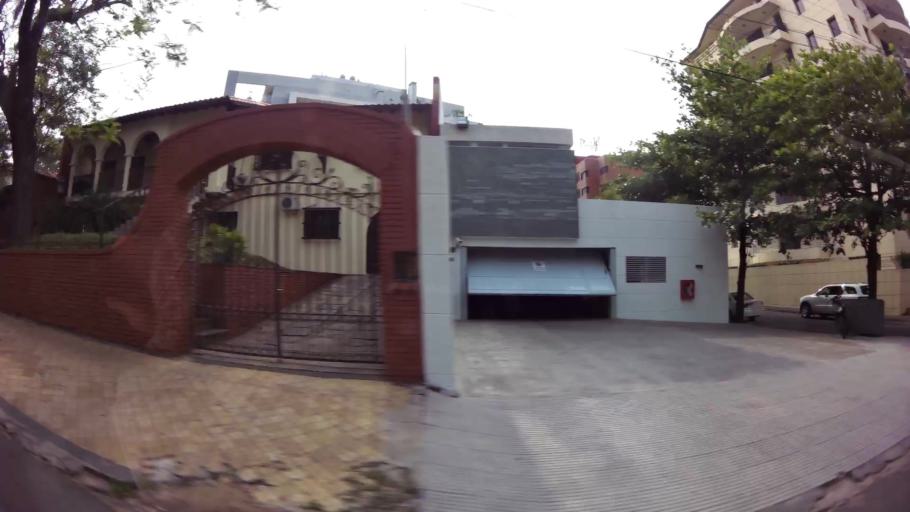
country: PY
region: Asuncion
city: Asuncion
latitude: -25.2913
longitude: -57.6105
